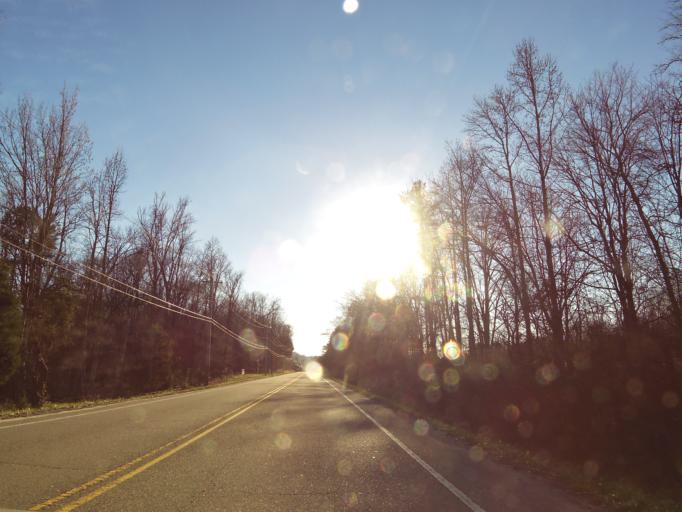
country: US
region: Tennessee
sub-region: Anderson County
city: Oak Ridge
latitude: 36.0577
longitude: -84.2367
